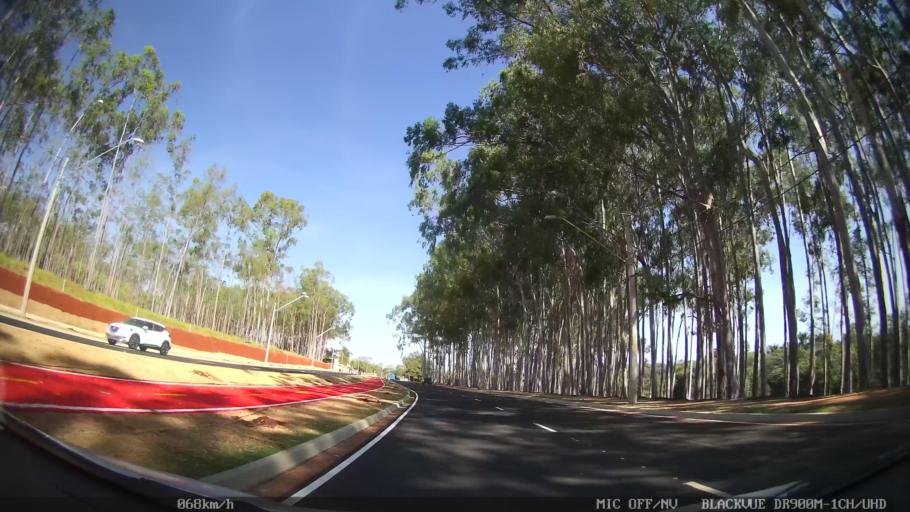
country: BR
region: Sao Paulo
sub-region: Ribeirao Preto
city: Ribeirao Preto
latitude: -21.2104
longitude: -47.8339
